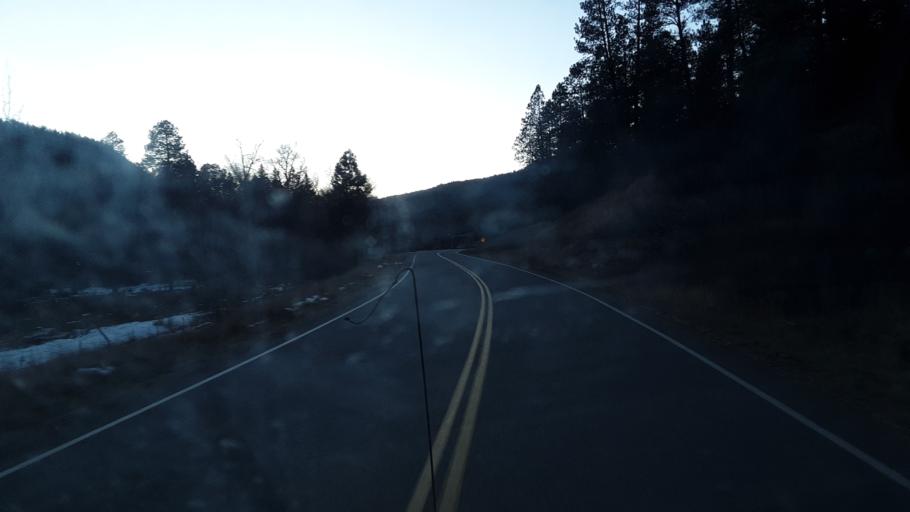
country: US
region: Colorado
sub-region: La Plata County
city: Bayfield
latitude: 37.3465
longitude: -107.6999
